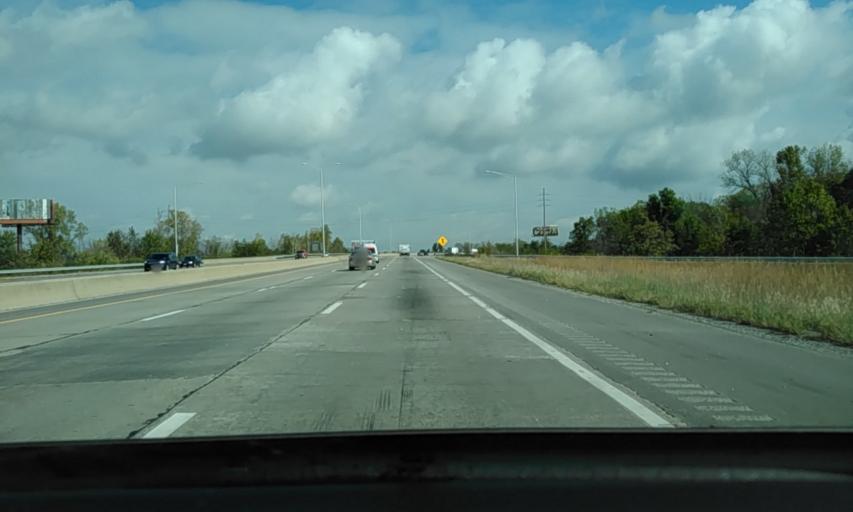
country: US
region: Illinois
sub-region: Saint Clair County
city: Washington Park
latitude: 38.6052
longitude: -90.0840
